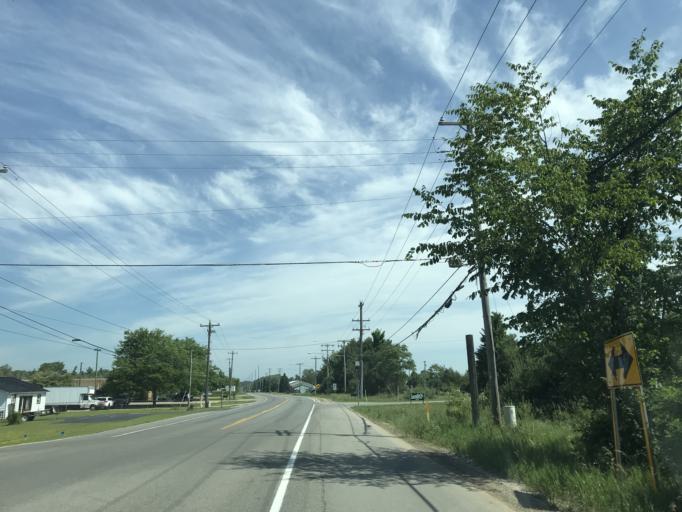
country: US
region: Michigan
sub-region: Grand Traverse County
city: Traverse City
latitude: 44.7153
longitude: -85.6261
